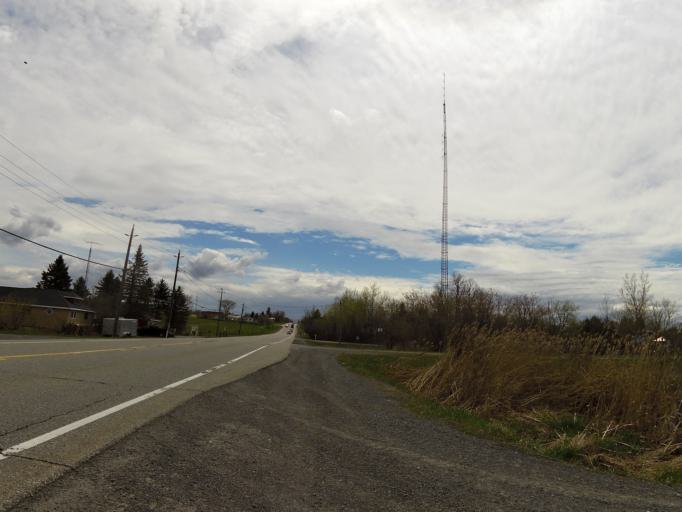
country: CA
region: Ontario
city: Hawkesbury
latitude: 45.5351
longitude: -74.6440
